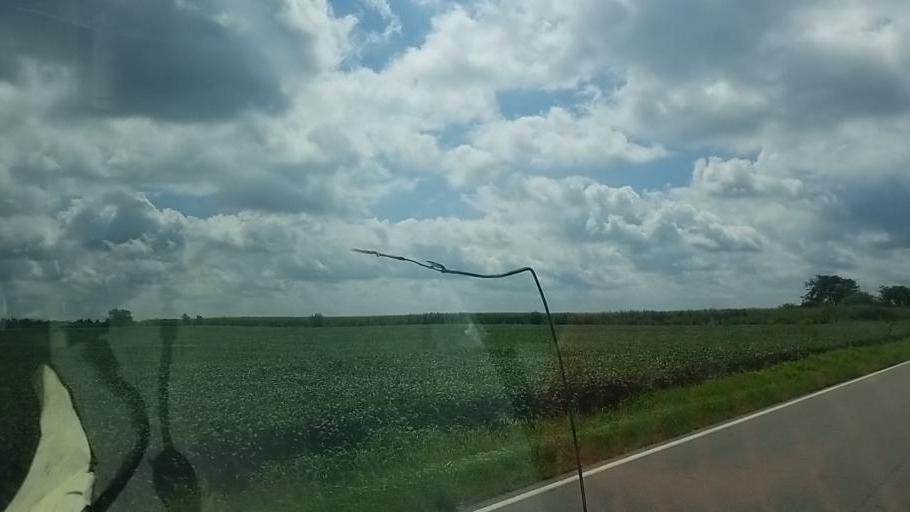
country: US
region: Ohio
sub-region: Fayette County
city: Jeffersonville
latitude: 39.6804
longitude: -83.5040
